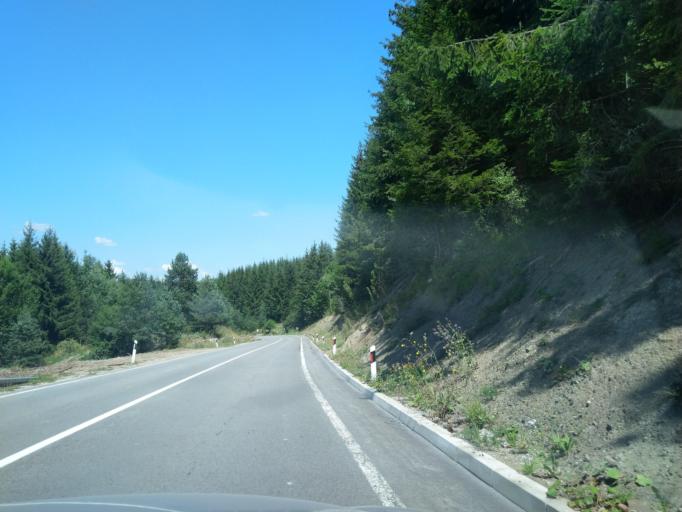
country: RS
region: Central Serbia
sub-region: Zlatiborski Okrug
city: Sjenica
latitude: 43.3173
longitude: 19.8927
